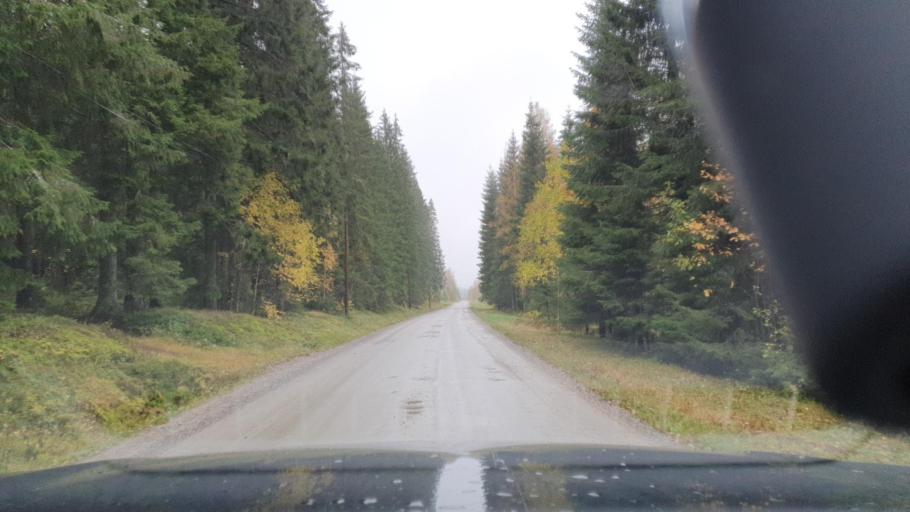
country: SE
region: Vaermland
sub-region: Arvika Kommun
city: Arvika
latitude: 59.7860
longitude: 12.7635
